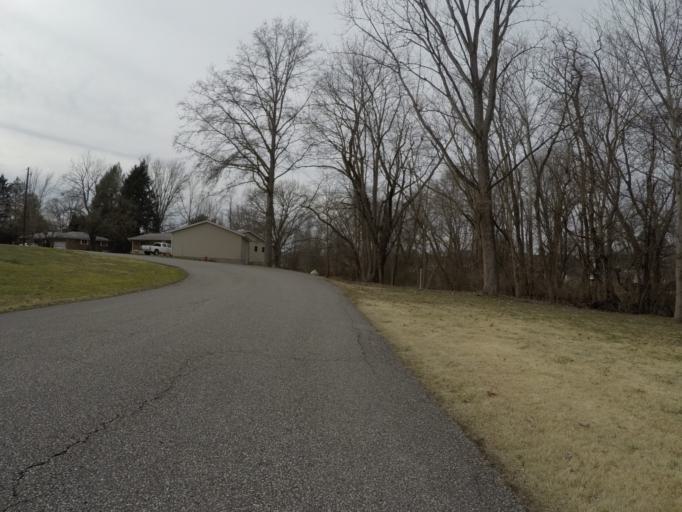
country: US
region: West Virginia
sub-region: Cabell County
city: Pea Ridge
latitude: 38.4483
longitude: -82.3454
